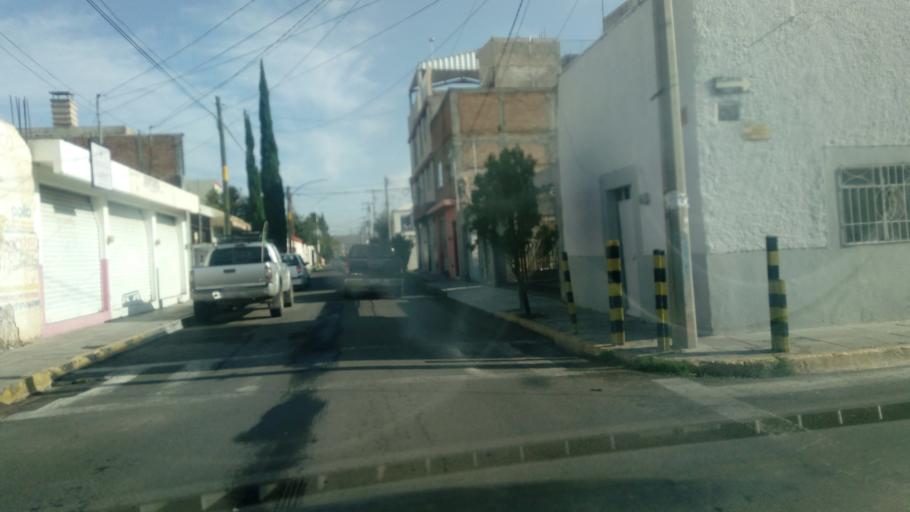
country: MX
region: Durango
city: Victoria de Durango
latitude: 24.0288
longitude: -104.6641
